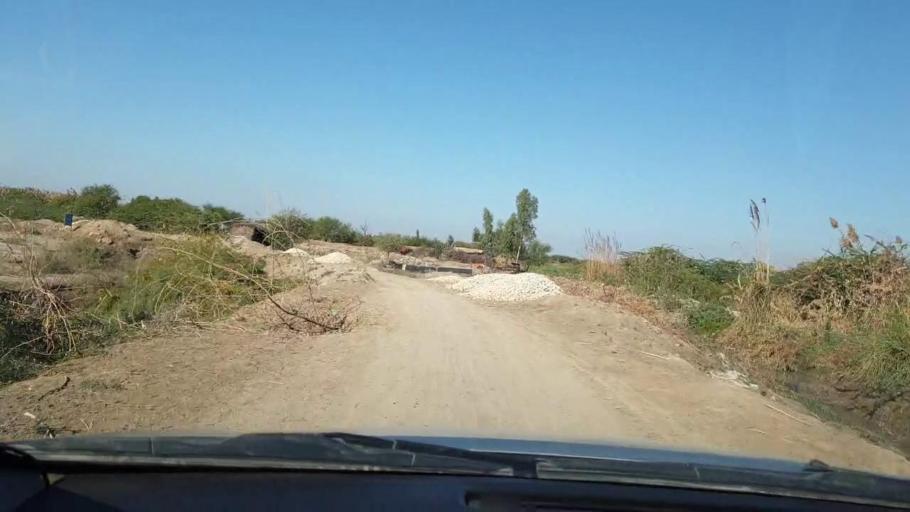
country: PK
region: Sindh
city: Berani
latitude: 25.7286
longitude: 68.9880
